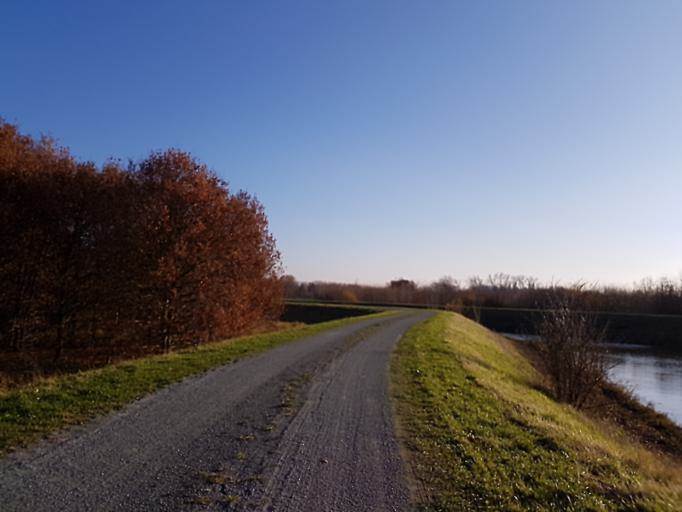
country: BE
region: Flanders
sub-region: Provincie Antwerpen
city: Bonheiden
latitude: 51.0076
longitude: 4.5323
